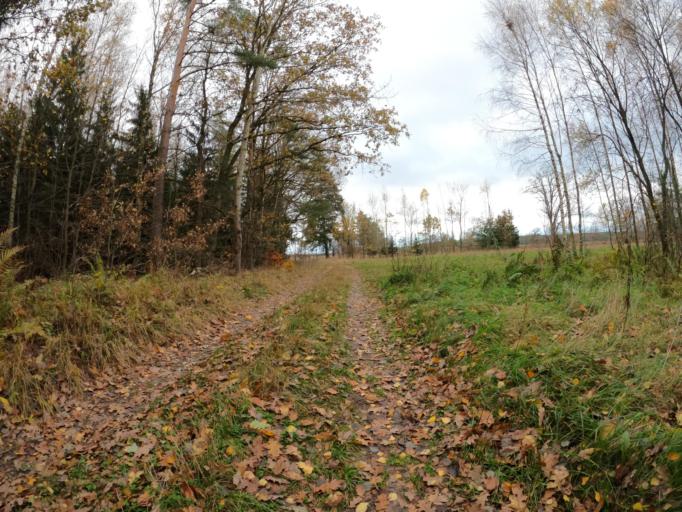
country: PL
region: West Pomeranian Voivodeship
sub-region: Powiat walecki
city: Miroslawiec
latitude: 53.3184
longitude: 16.1171
